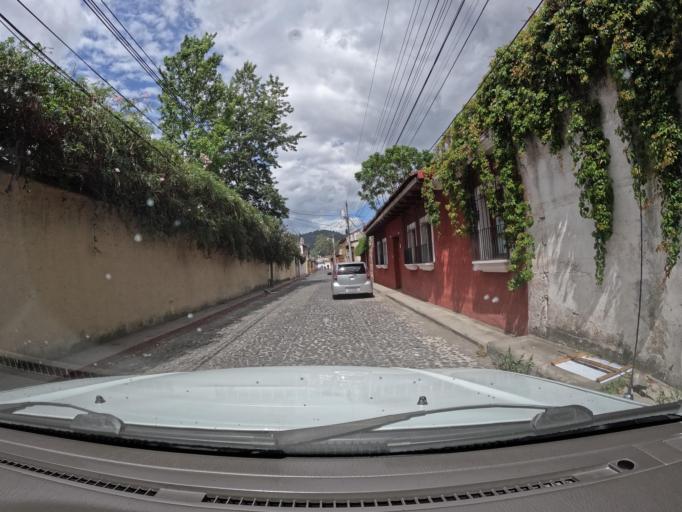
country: GT
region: Sacatepequez
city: Antigua Guatemala
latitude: 14.5525
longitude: -90.7423
